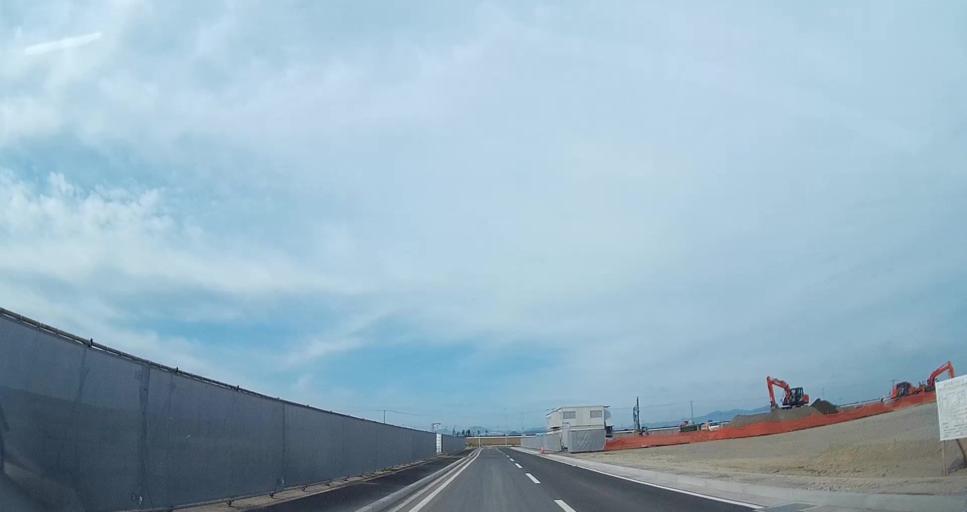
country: JP
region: Miyagi
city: Sendai
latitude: 38.1845
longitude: 140.9550
